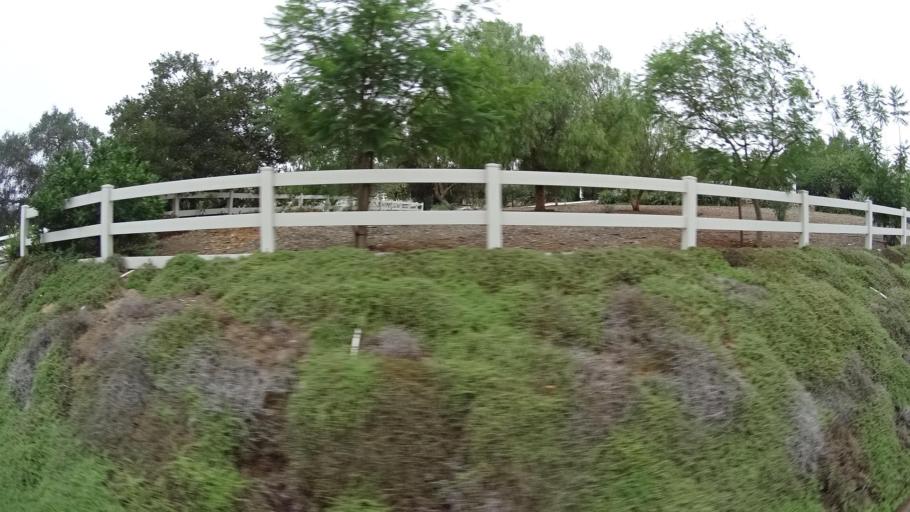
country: US
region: California
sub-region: San Diego County
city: Fallbrook
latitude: 33.3853
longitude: -117.2083
